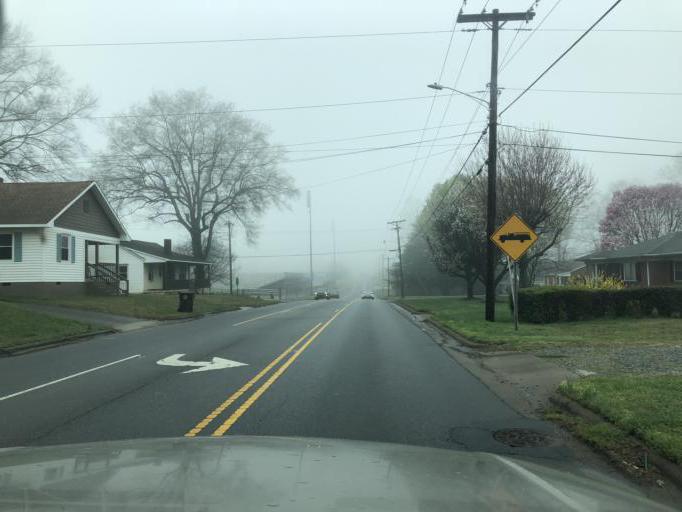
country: US
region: North Carolina
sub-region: Gaston County
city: Cherryville
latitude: 35.3842
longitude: -81.3733
